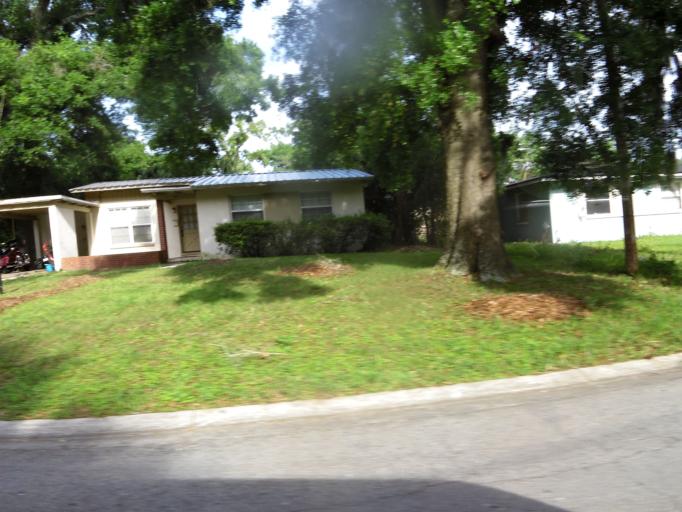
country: US
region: Florida
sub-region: Duval County
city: Jacksonville
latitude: 30.3295
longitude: -81.5914
